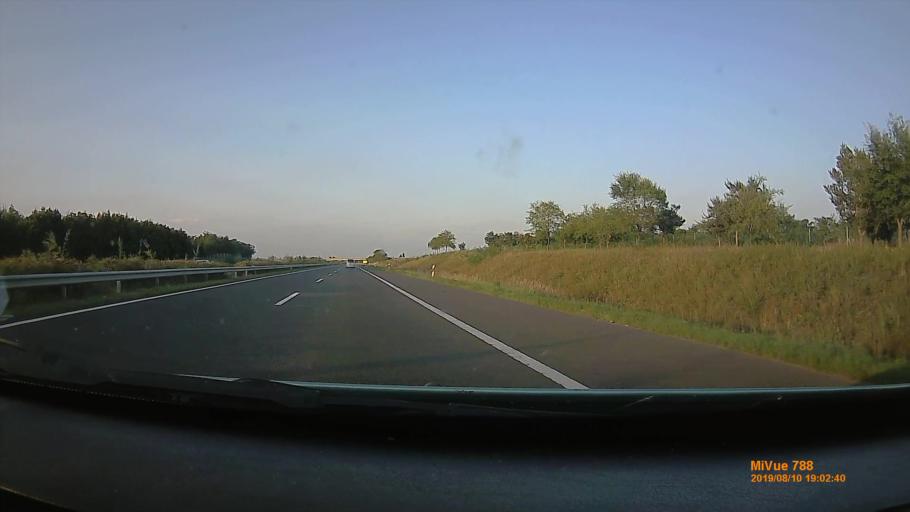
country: HU
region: Borsod-Abauj-Zemplen
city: Emod
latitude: 47.9403
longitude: 20.8685
